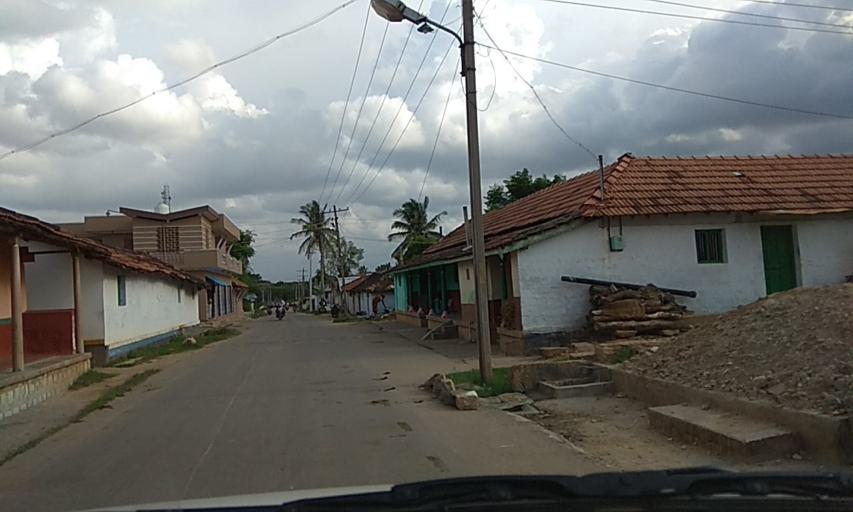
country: IN
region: Karnataka
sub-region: Chamrajnagar
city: Gundlupet
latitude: 11.8908
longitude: 76.7463
